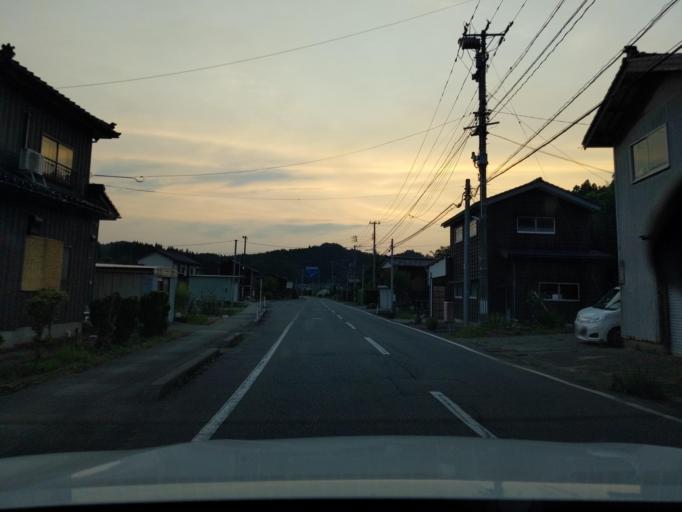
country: JP
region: Niigata
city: Kashiwazaki
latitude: 37.4492
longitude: 138.6394
